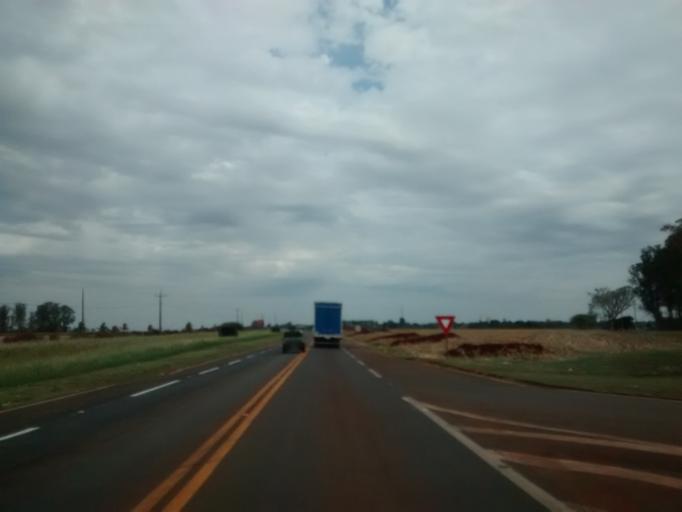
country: BR
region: Parana
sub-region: Peabiru
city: Peabiru
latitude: -23.8934
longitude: -52.3266
